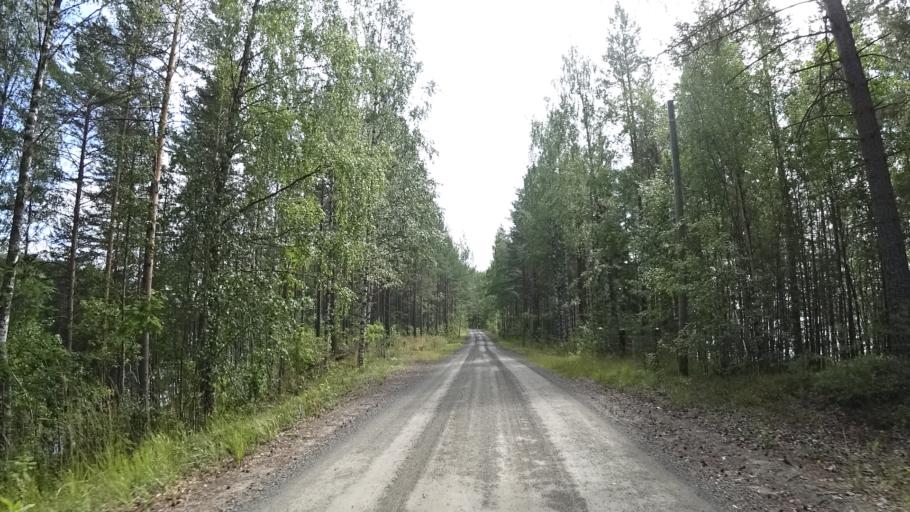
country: FI
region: North Karelia
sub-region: Joensuu
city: Pyhaeselkae
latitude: 62.3790
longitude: 29.8095
